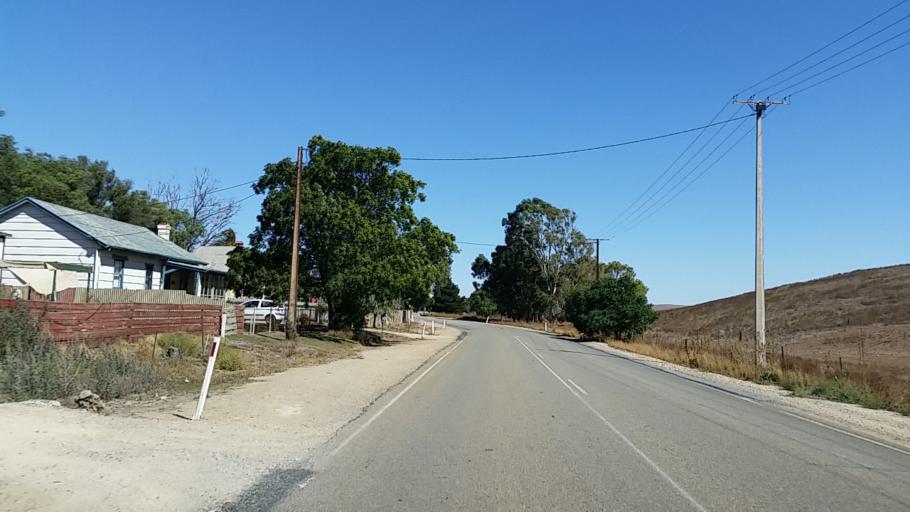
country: AU
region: South Australia
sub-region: Clare and Gilbert Valleys
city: Clare
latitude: -33.6750
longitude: 138.9174
